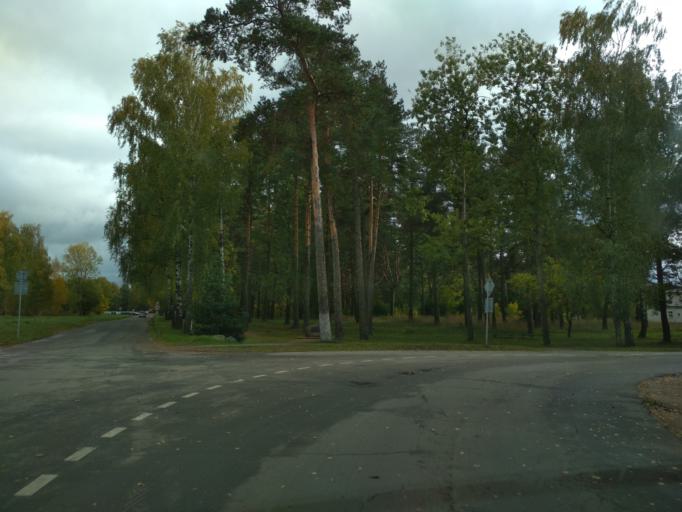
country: BY
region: Minsk
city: Blon'
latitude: 53.5048
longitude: 28.1716
